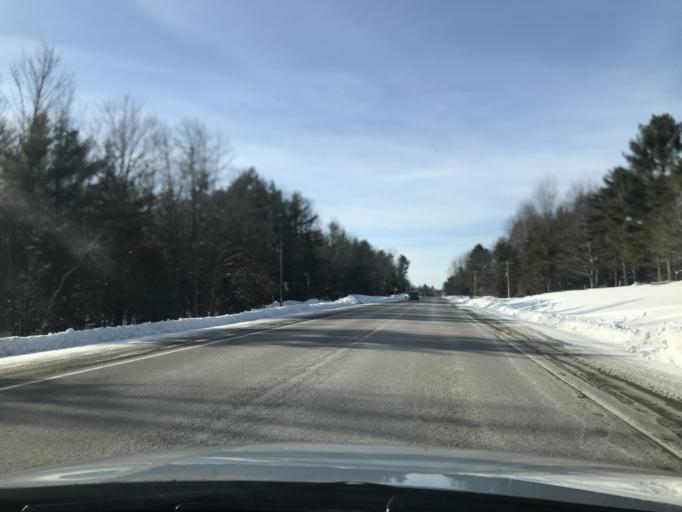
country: US
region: Wisconsin
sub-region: Oconto County
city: Gillett
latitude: 45.1289
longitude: -88.4165
